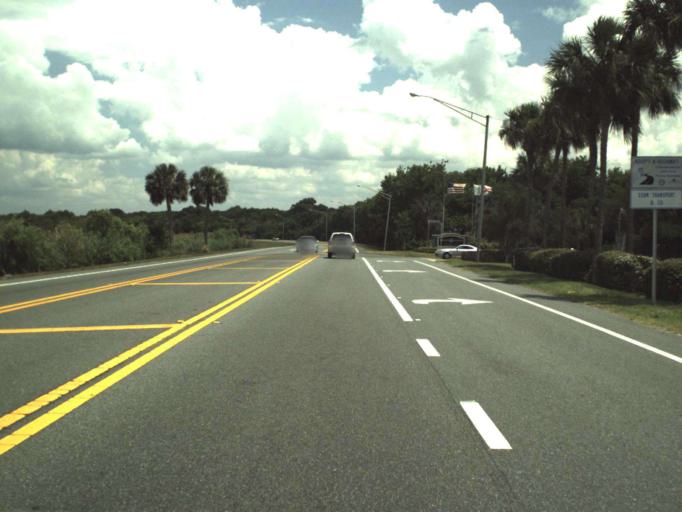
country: US
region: Florida
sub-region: Seminole County
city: Sanford
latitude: 28.8195
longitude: -81.2906
